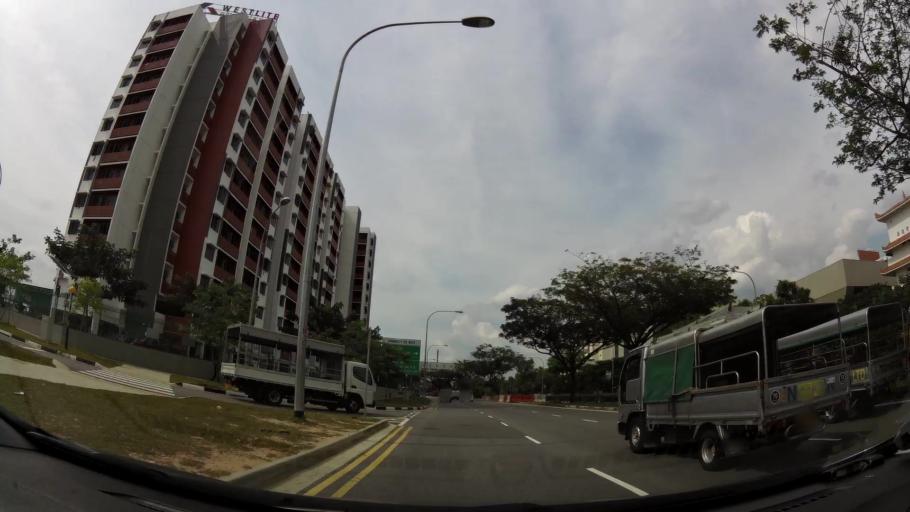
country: MY
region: Johor
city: Johor Bahru
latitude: 1.4612
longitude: 103.8101
